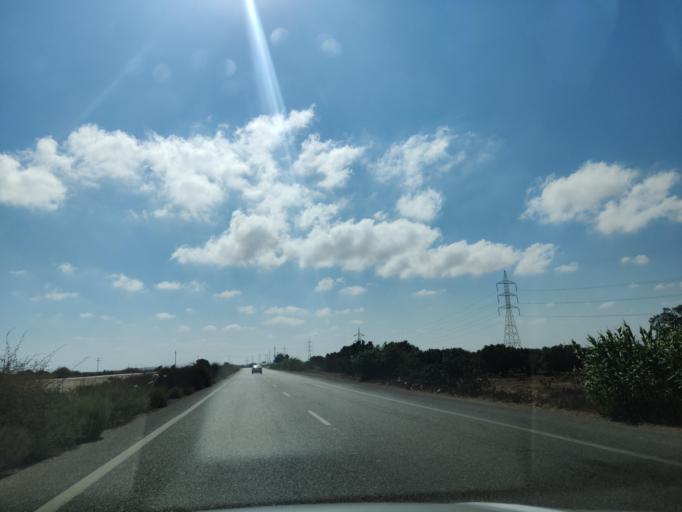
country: EG
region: Muhafazat Matruh
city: Al `Alamayn
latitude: 31.0541
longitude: 28.2871
